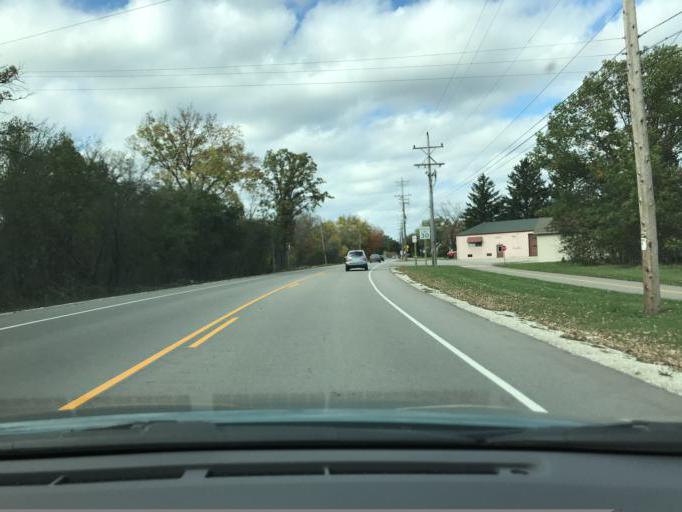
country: US
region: Wisconsin
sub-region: Racine County
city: Burlington
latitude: 42.6738
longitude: -88.2664
